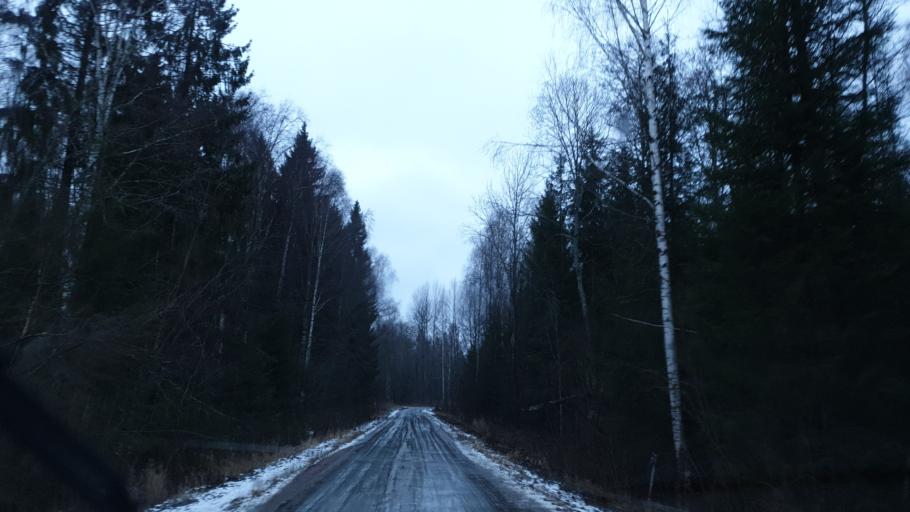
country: SE
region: Uppsala
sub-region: Tierps Kommun
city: Tierp
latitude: 60.3479
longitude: 17.4657
